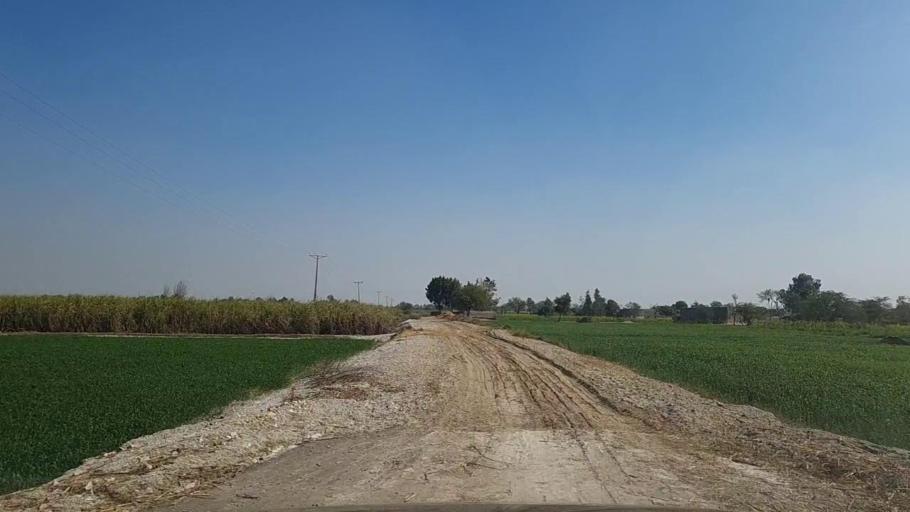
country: PK
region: Sindh
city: Bandhi
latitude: 26.5555
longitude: 68.3607
